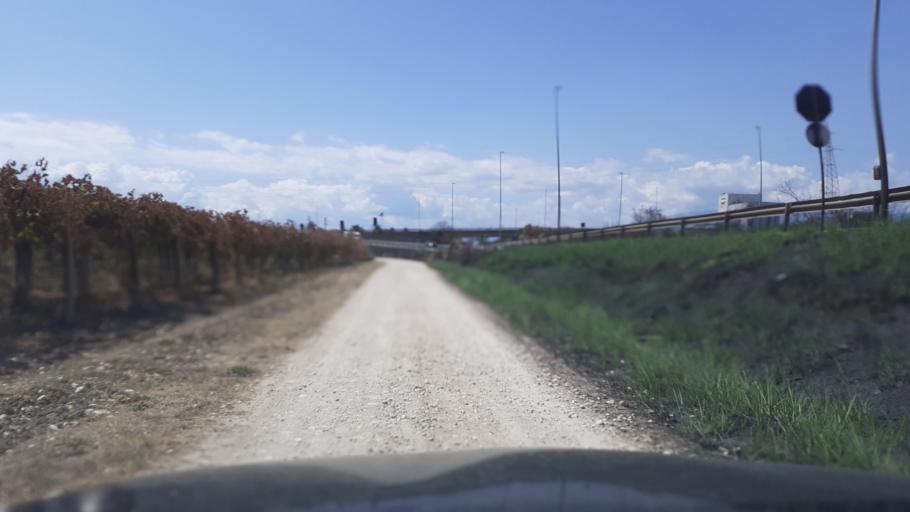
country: IT
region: Abruzzo
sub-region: Provincia di Chieti
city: Fossacesia
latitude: 42.2170
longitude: 14.4976
